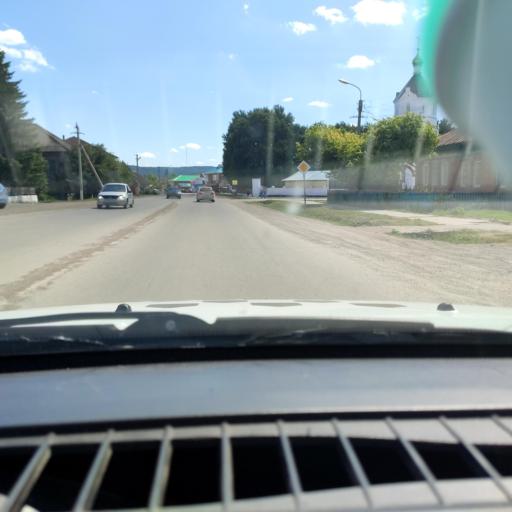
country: RU
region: Bashkortostan
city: Mesyagutovo
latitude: 55.5335
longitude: 58.2475
